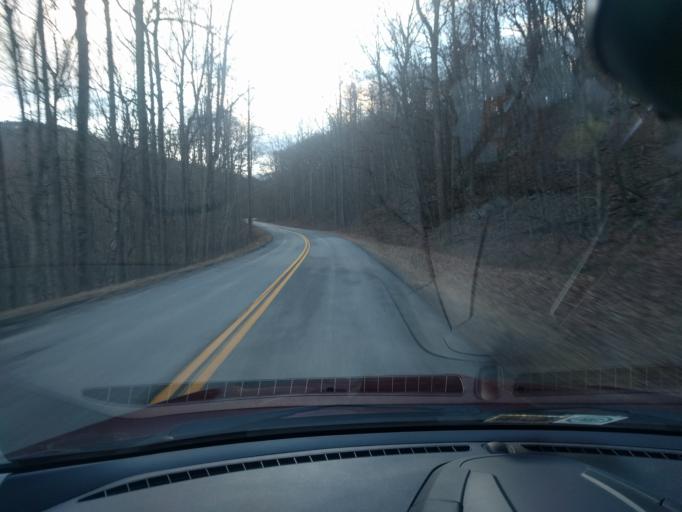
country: US
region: Virginia
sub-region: Botetourt County
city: Buchanan
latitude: 37.4619
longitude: -79.6338
